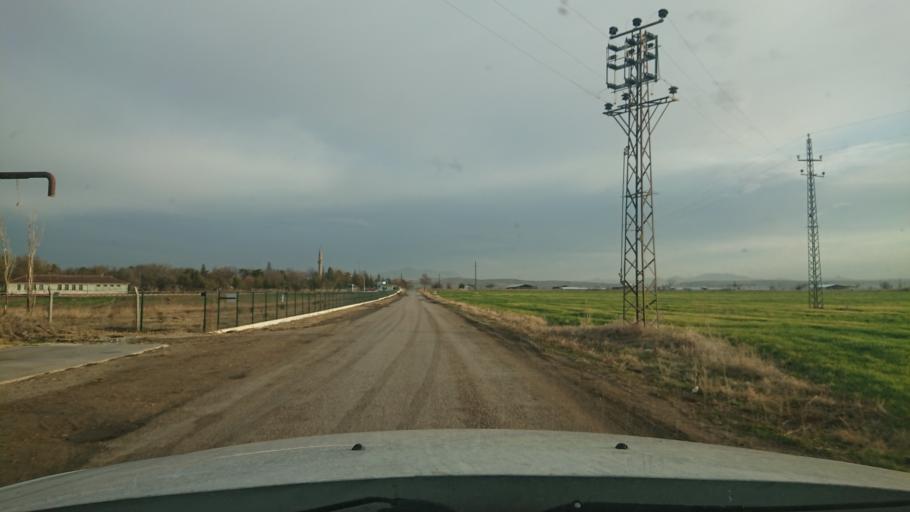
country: TR
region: Aksaray
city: Yesilova
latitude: 38.4548
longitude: 33.8382
